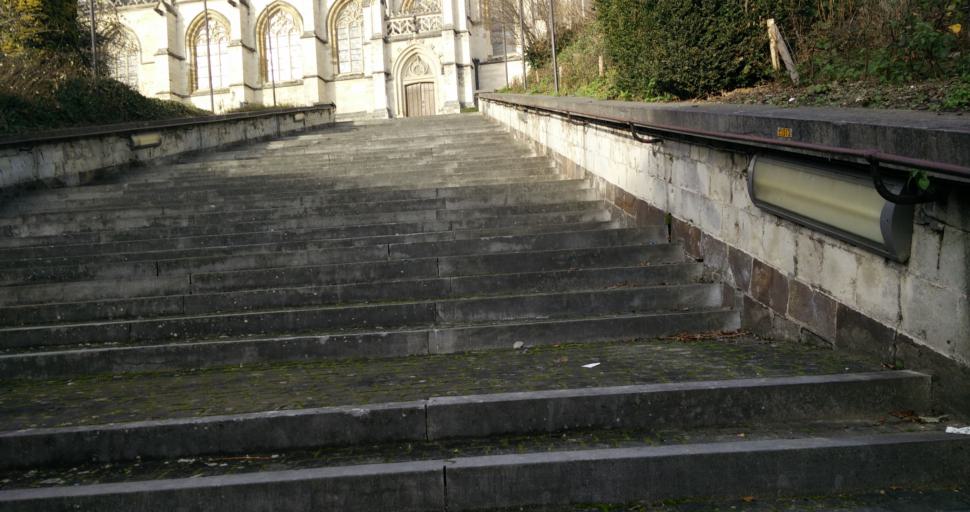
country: BE
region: Flanders
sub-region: Provincie Vlaams-Brabant
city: Sint-Genesius-Rode
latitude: 50.7426
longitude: 4.3364
